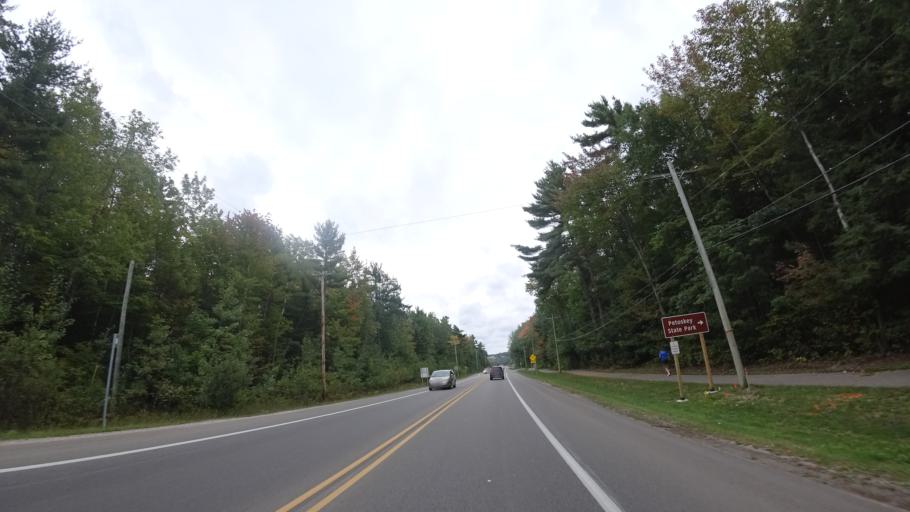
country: US
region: Michigan
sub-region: Emmet County
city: Petoskey
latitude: 45.4096
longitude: -84.9022
